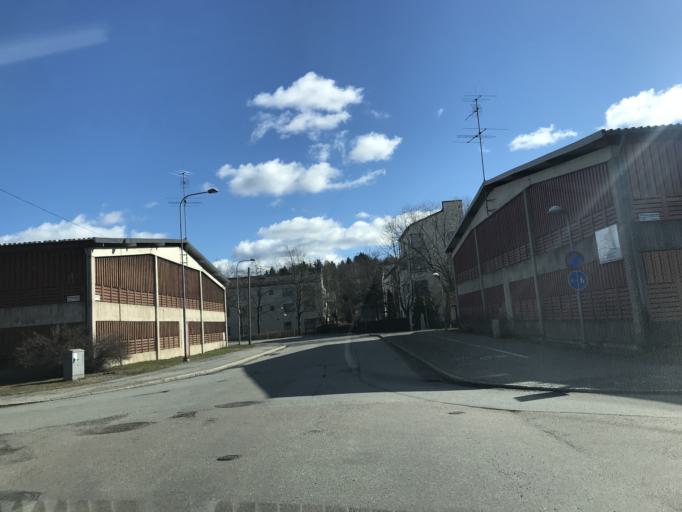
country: SE
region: Stockholm
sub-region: Stockholms Kommun
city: Kista
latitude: 59.3964
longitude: 17.9398
